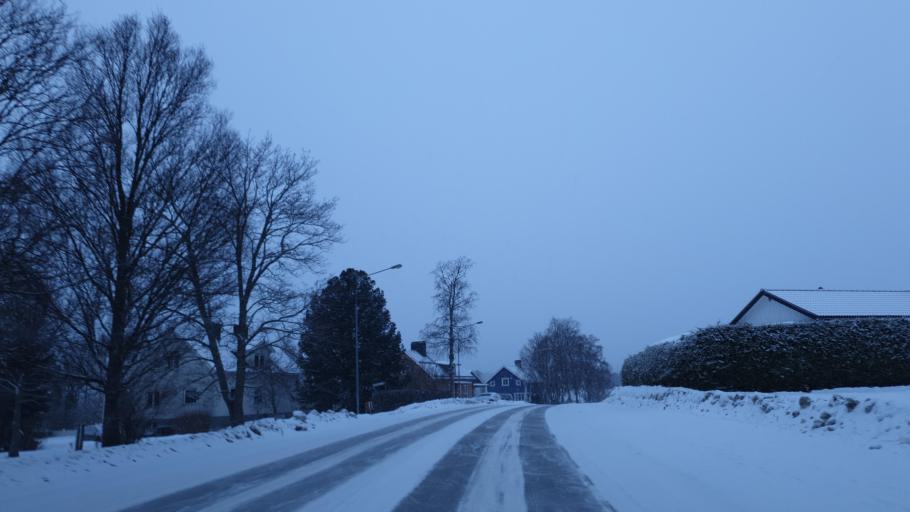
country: SE
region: Vaesternorrland
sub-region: OErnskoeldsviks Kommun
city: Ornskoldsvik
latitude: 63.2972
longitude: 18.6300
